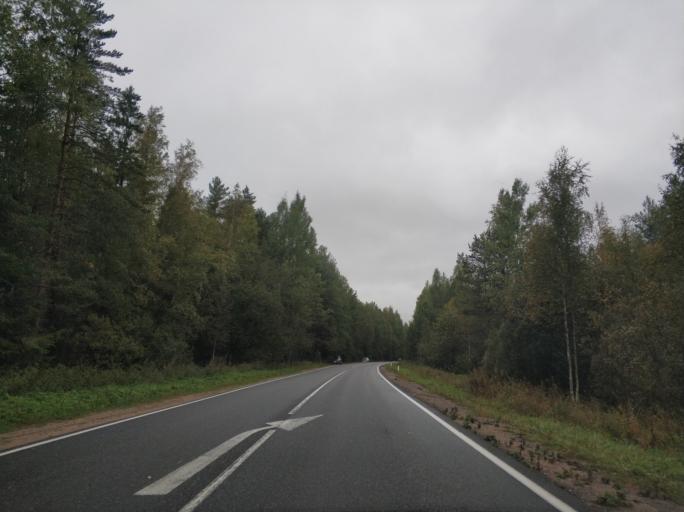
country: RU
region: Leningrad
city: Borisova Griva
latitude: 60.1597
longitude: 30.9244
